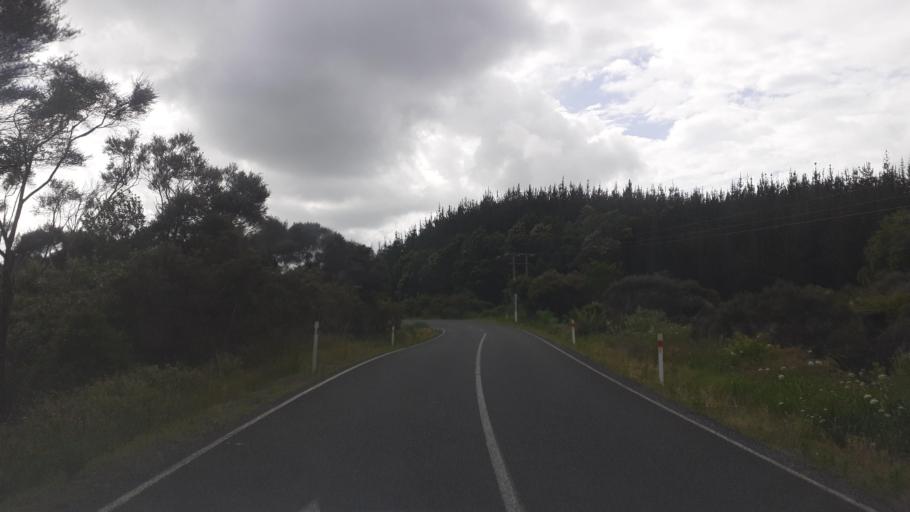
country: NZ
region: Northland
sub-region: Far North District
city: Kerikeri
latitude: -35.2252
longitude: 174.0091
